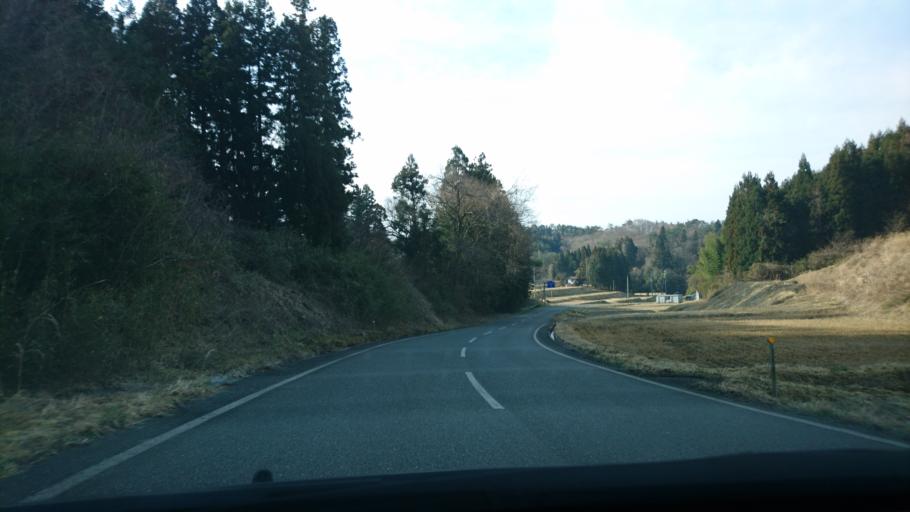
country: JP
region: Iwate
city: Ichinoseki
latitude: 38.8359
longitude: 141.2190
